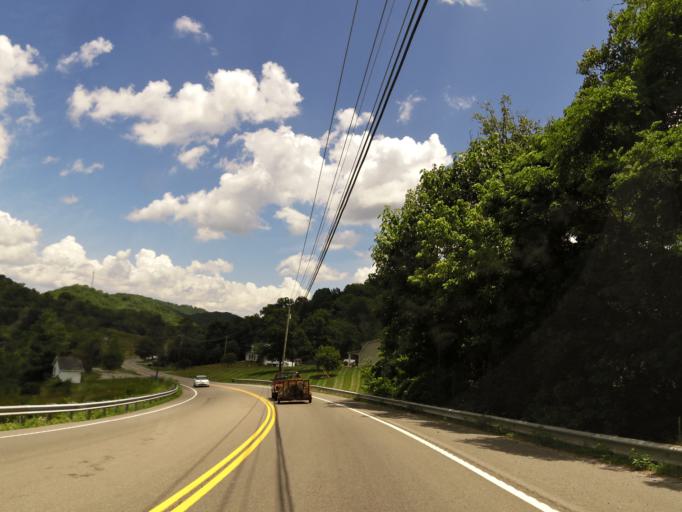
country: US
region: Tennessee
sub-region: Union County
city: Maynardville
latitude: 36.2823
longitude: -83.7624
